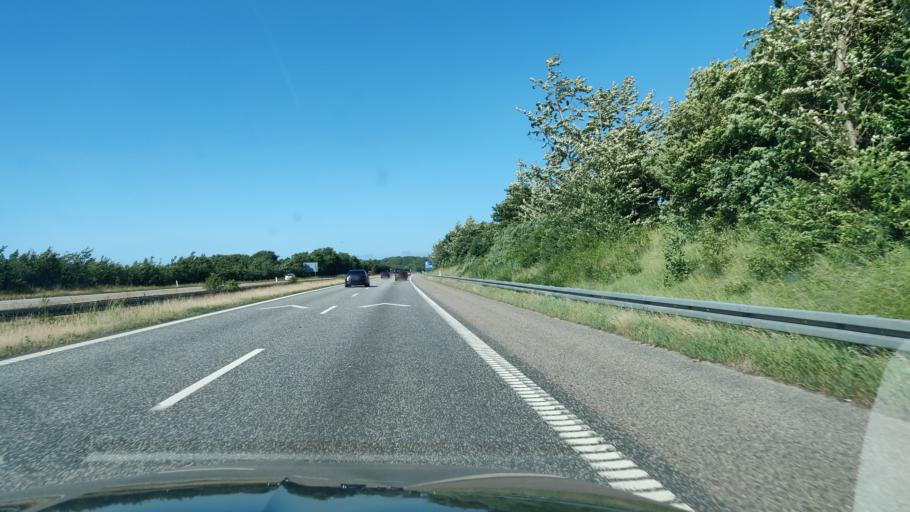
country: DK
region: North Denmark
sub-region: Rebild Kommune
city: Stovring
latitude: 56.8333
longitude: 9.7305
